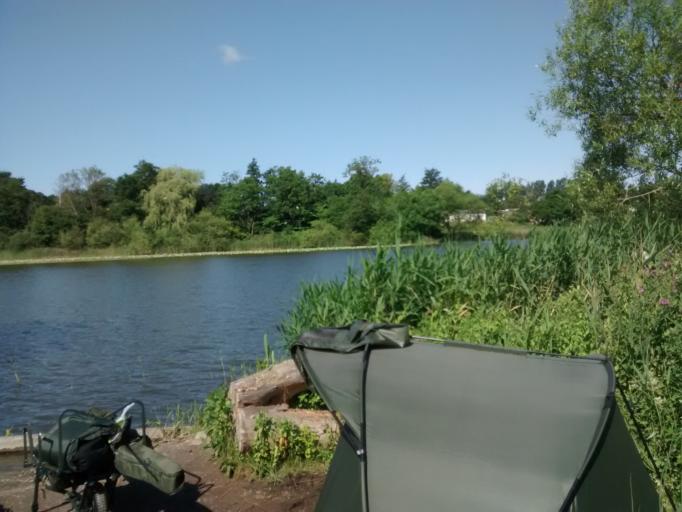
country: DK
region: Zealand
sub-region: Soro Kommune
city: Soro
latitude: 55.4447
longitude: 11.5514
